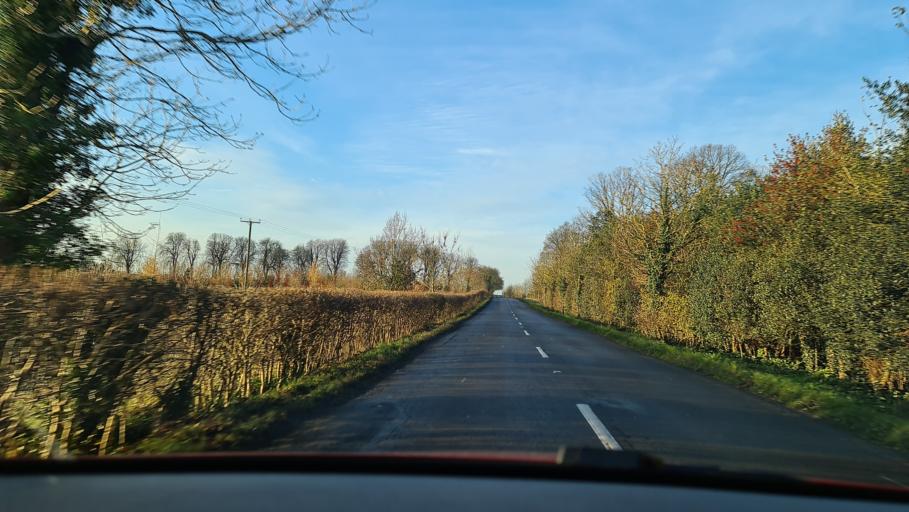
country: GB
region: England
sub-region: Buckinghamshire
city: Waddesdon
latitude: 51.8243
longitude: -0.9147
